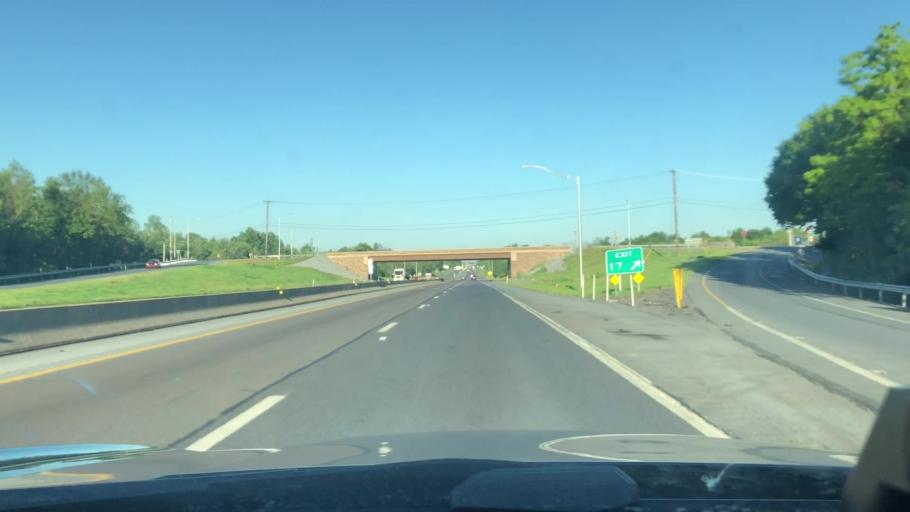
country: US
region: Pennsylvania
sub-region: Schuylkill County
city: Lake Wynonah
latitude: 40.4919
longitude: -76.2210
